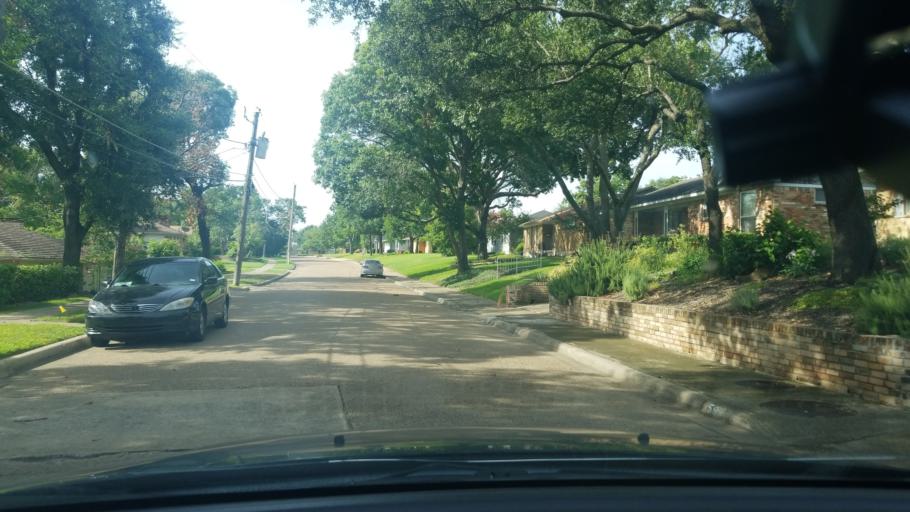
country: US
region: Texas
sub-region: Dallas County
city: Highland Park
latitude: 32.7982
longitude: -96.6990
